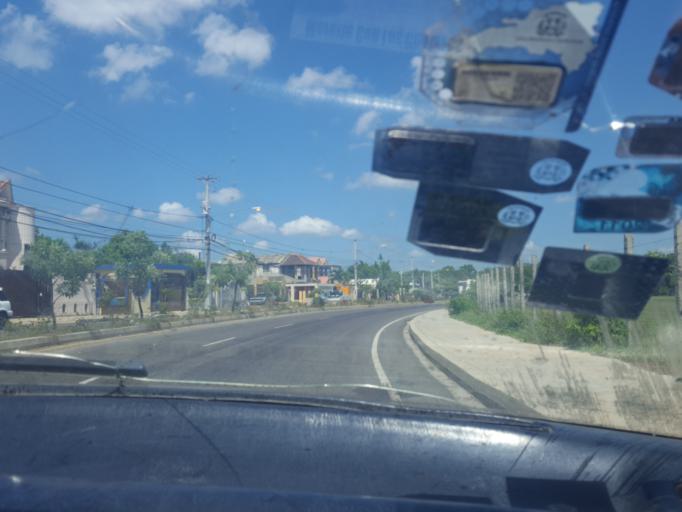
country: DO
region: Santiago
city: Santiago de los Caballeros
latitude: 19.4953
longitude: -70.7011
